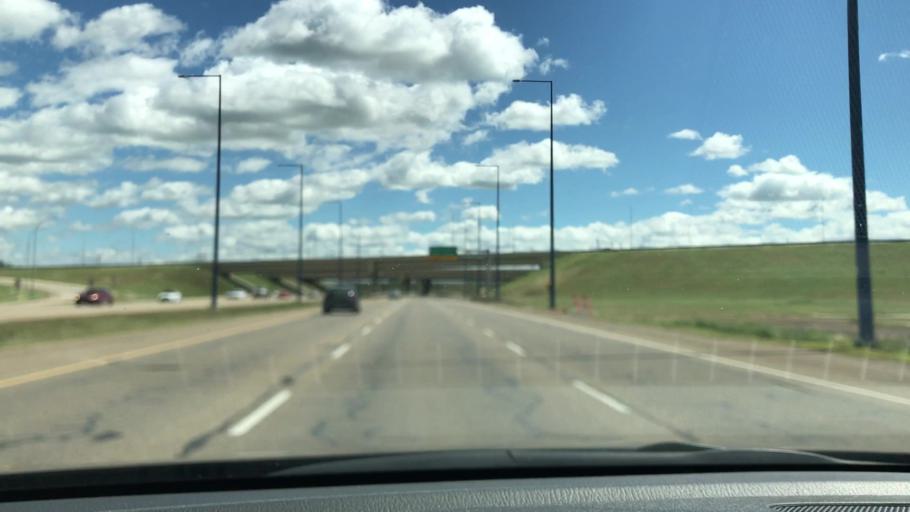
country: CA
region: Alberta
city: Edmonton
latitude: 53.4401
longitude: -113.4921
